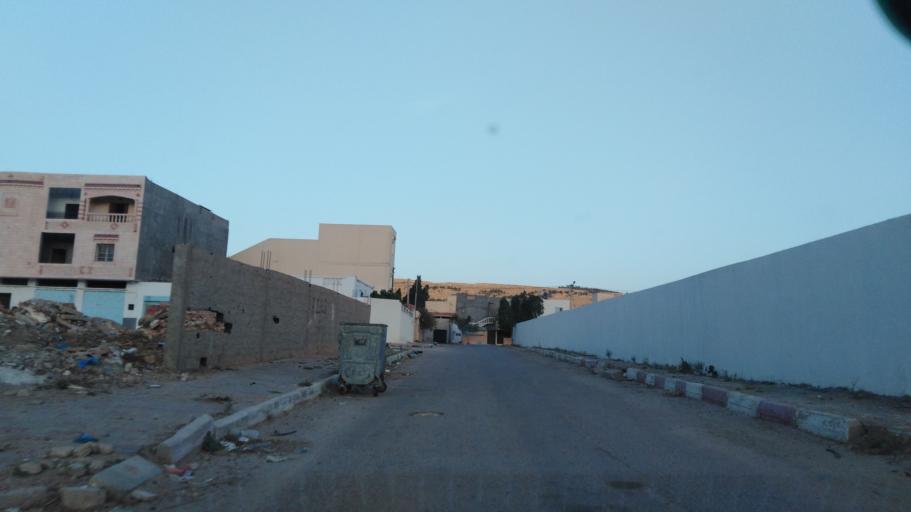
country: TN
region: Tataouine
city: Tataouine
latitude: 32.9403
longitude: 10.4544
